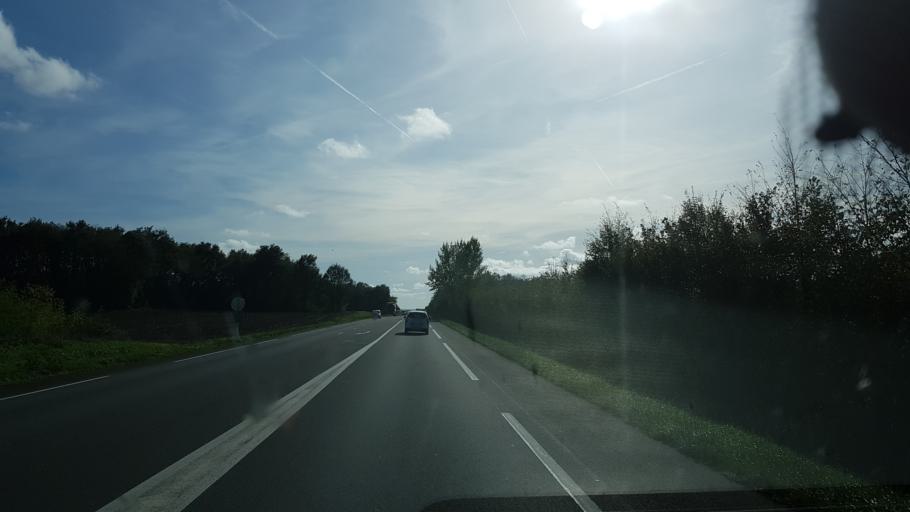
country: FR
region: Poitou-Charentes
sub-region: Departement de la Charente
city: Chasseneuil-sur-Bonnieure
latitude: 45.8539
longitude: 0.4636
